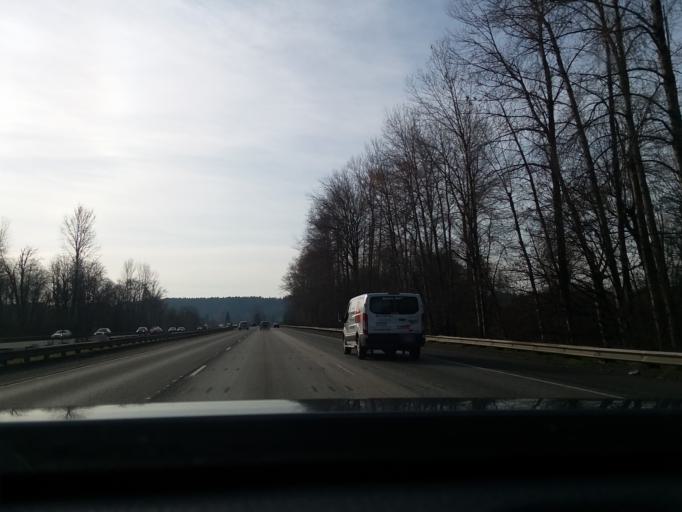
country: US
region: Washington
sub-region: Thurston County
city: Tanglewilde-Thompson Place
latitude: 47.0710
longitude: -122.7065
